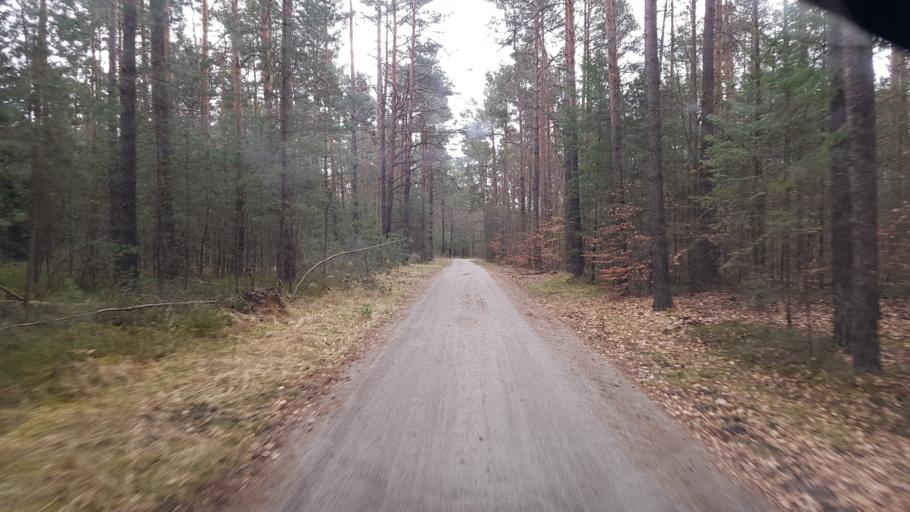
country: DE
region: Brandenburg
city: Finsterwalde
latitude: 51.5723
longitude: 13.7041
